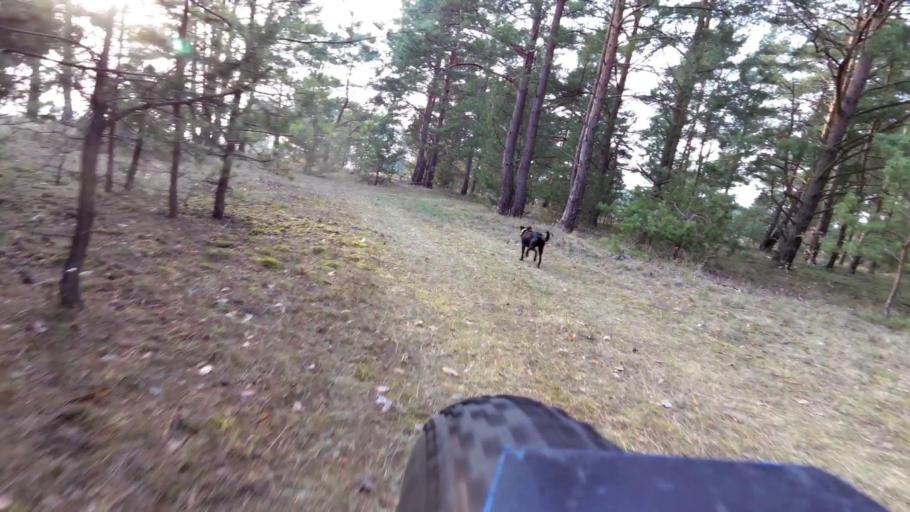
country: DE
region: Brandenburg
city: Ziltendorf
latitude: 52.2720
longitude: 14.6879
